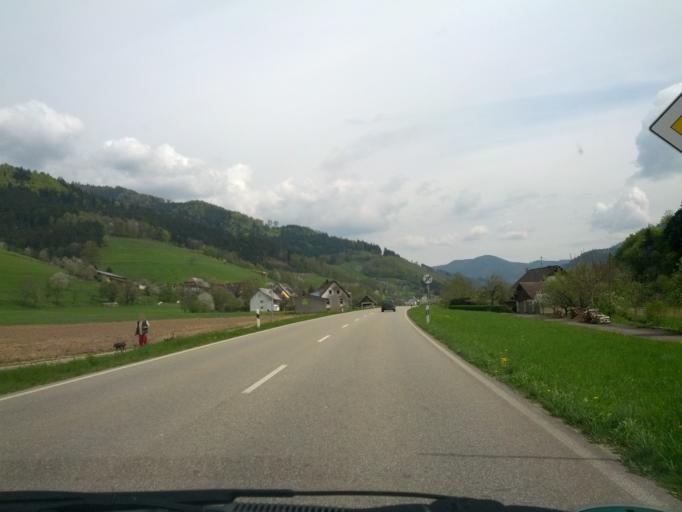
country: DE
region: Baden-Wuerttemberg
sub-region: Freiburg Region
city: Gutach im Breisgau
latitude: 48.1189
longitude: 8.0179
